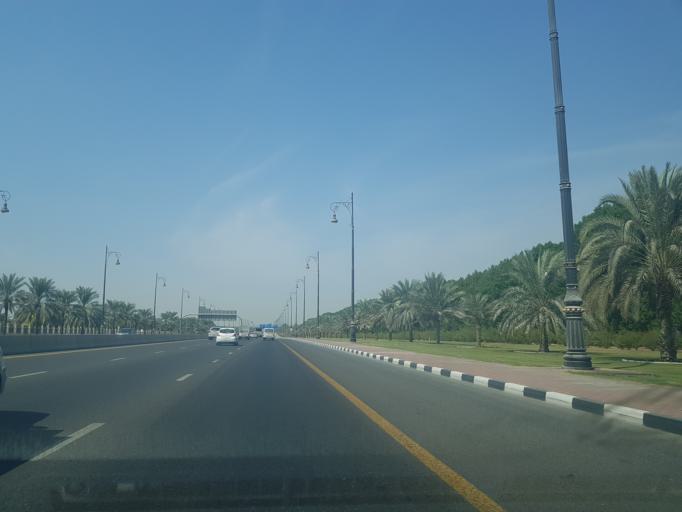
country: AE
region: Ash Shariqah
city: Sharjah
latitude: 25.3153
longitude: 55.5353
